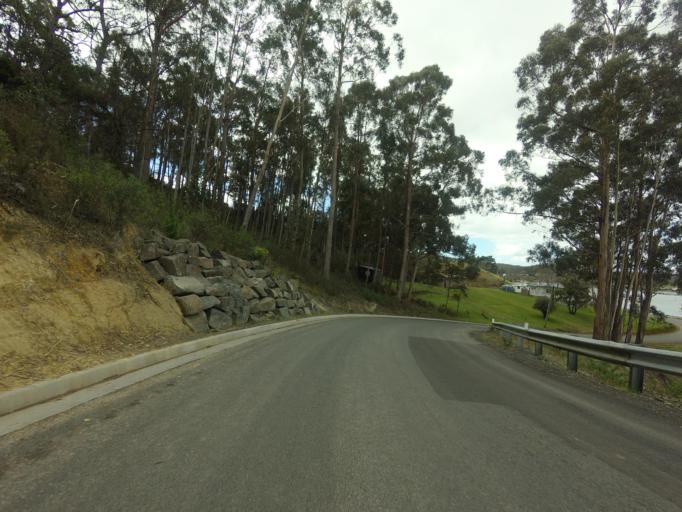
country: AU
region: Tasmania
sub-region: Huon Valley
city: Geeveston
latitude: -43.4337
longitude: 146.9667
